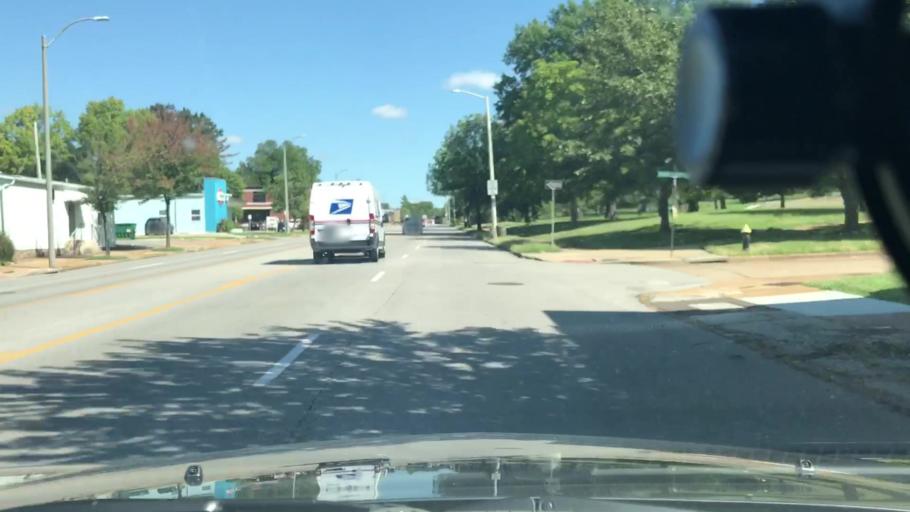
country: US
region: Missouri
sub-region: Saint Louis County
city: Maplewood
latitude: 38.5992
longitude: -90.2923
